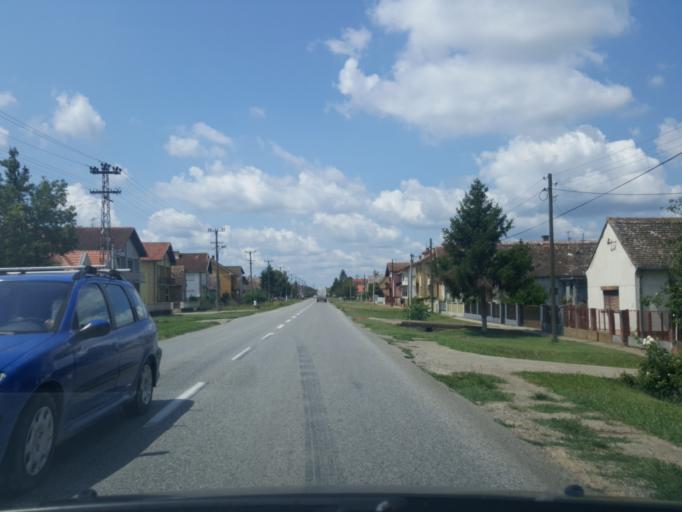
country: RS
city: Glusci
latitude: 44.9269
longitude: 19.5516
